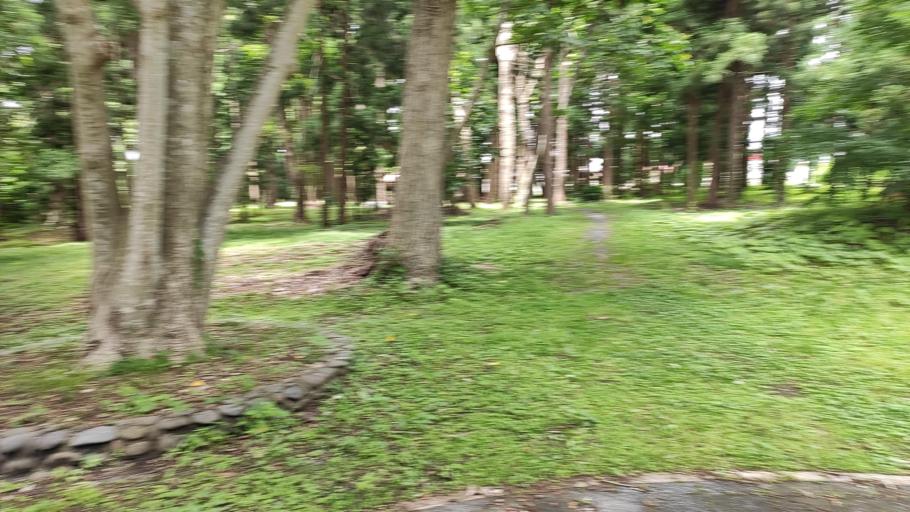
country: JP
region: Iwate
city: Kitakami
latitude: 39.2912
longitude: 141.0891
